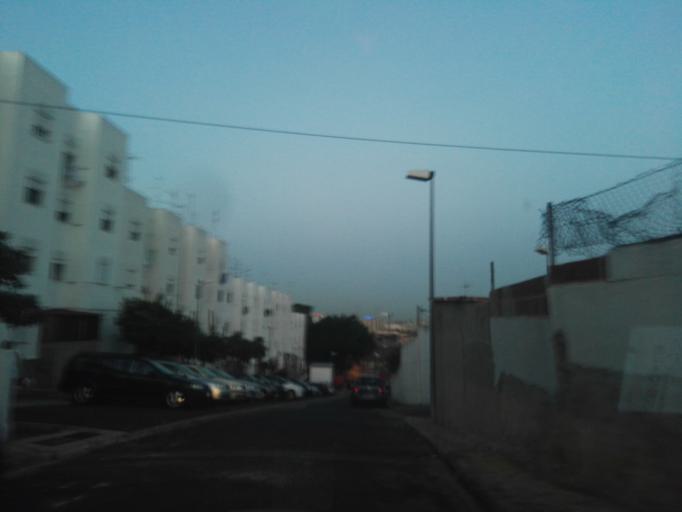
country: PT
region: Lisbon
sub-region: Odivelas
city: Pontinha
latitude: 38.7327
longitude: -9.1738
